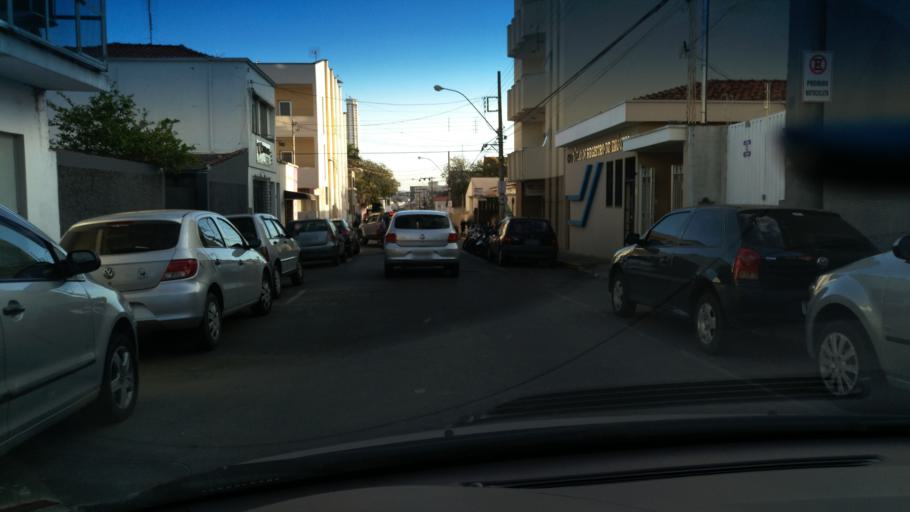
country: BR
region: Minas Gerais
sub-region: Andradas
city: Andradas
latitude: -22.0703
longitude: -46.5724
